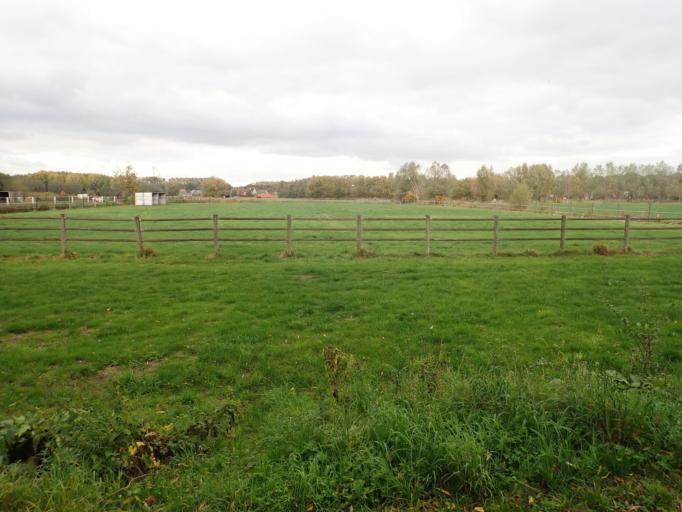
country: BE
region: Flanders
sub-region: Provincie Antwerpen
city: Willebroek
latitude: 51.0606
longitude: 4.3792
